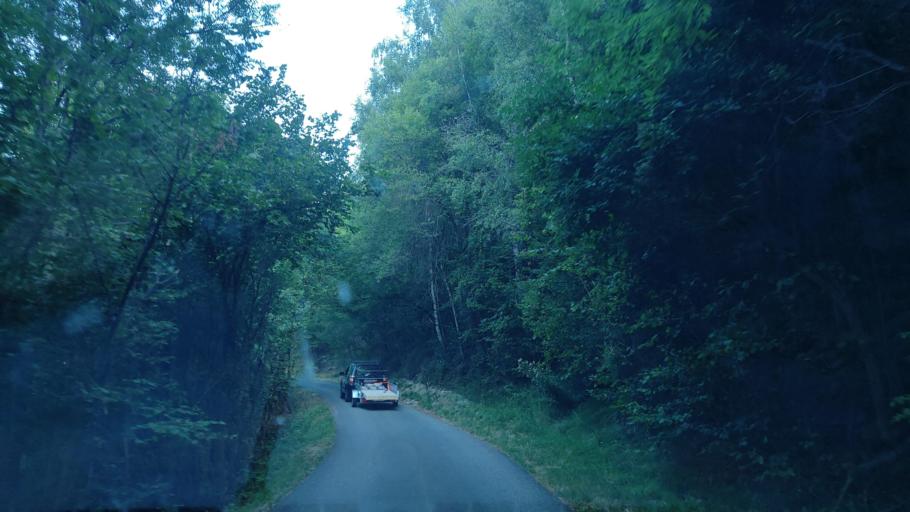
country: FR
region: Rhone-Alpes
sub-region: Departement de la Savoie
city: Val Thorens
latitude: 45.2128
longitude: 6.5651
